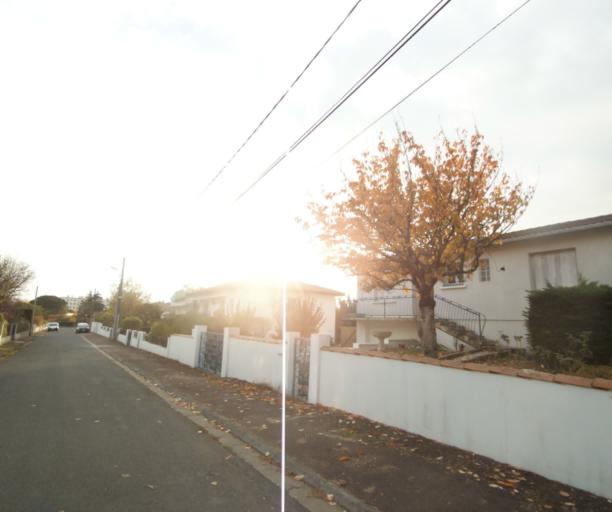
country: FR
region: Poitou-Charentes
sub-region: Departement de la Charente-Maritime
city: Saintes
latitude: 45.7524
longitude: -0.6462
